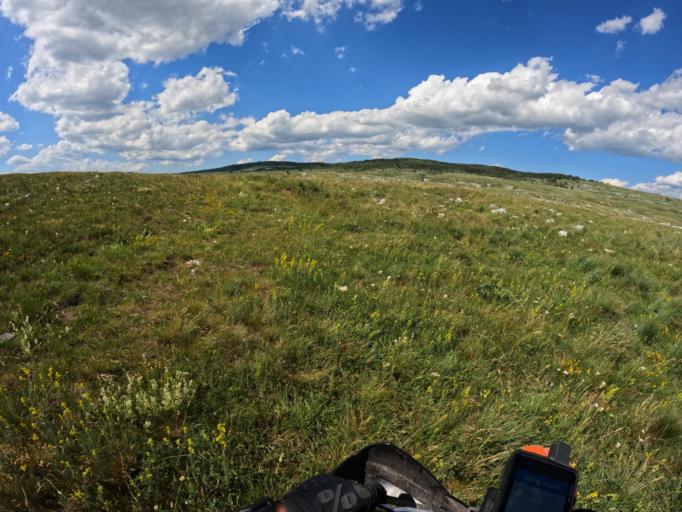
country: BA
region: Federation of Bosnia and Herzegovina
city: Glamoc
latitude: 44.0221
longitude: 17.0188
